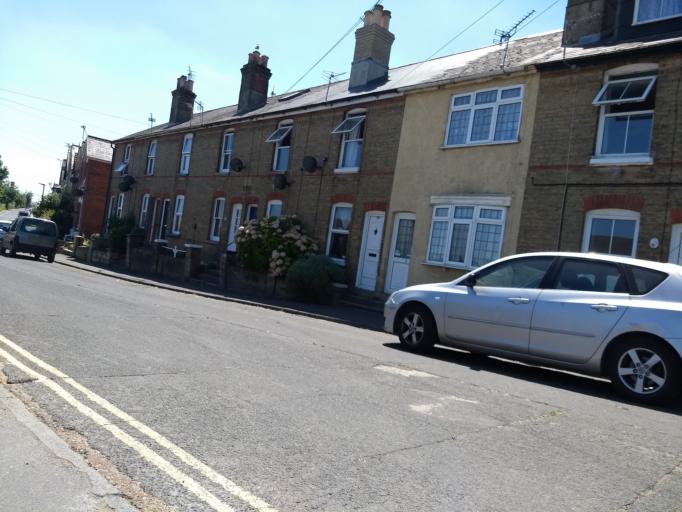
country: GB
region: England
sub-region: Isle of Wight
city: East Cowes
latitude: 50.7538
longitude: -1.2960
